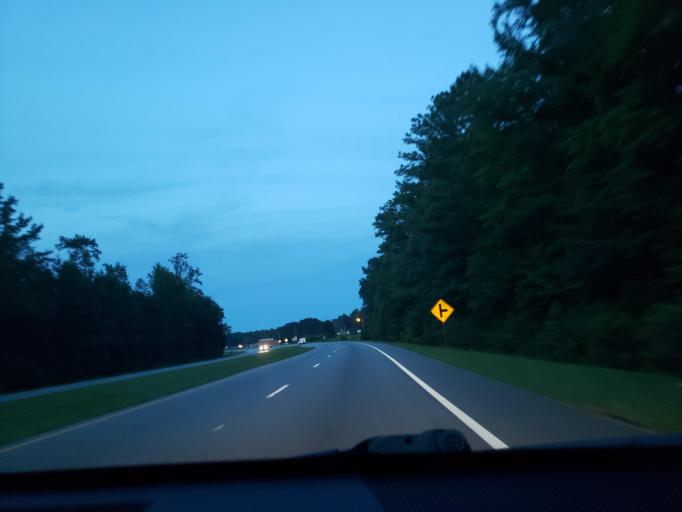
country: US
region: Virginia
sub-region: City of Franklin
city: Franklin
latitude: 36.6543
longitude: -76.8236
